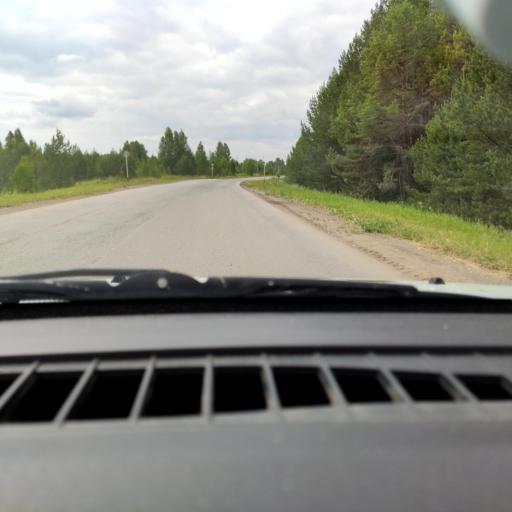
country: RU
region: Perm
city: Orda
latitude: 57.1489
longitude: 56.7589
